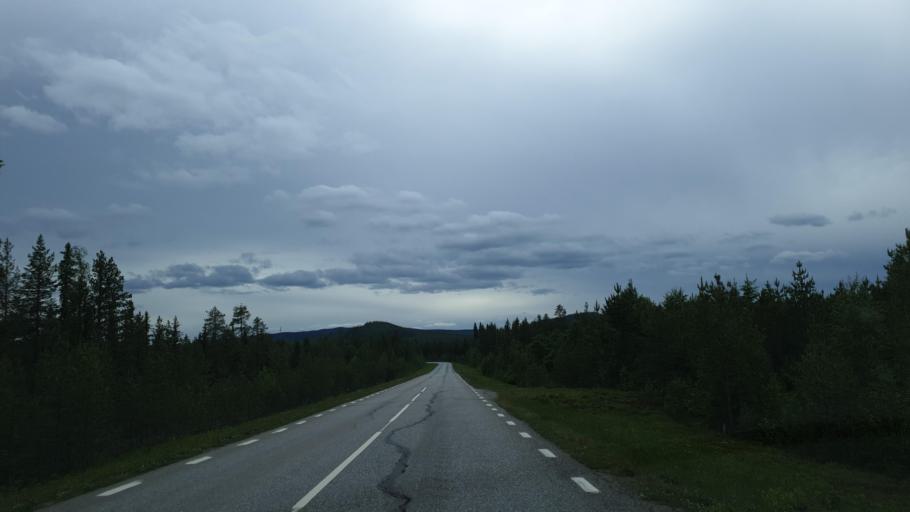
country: SE
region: Vaesterbotten
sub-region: Sorsele Kommun
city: Sorsele
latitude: 65.5313
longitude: 17.3930
